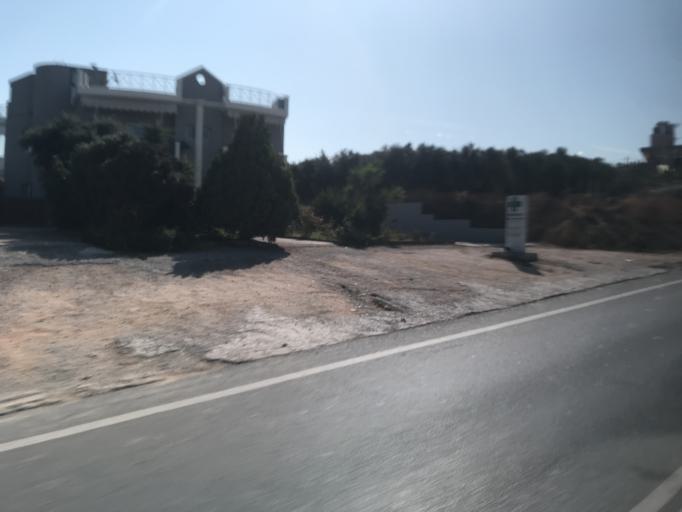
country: GR
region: Crete
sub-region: Nomos Irakleiou
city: Gazi
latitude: 35.3110
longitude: 25.0911
